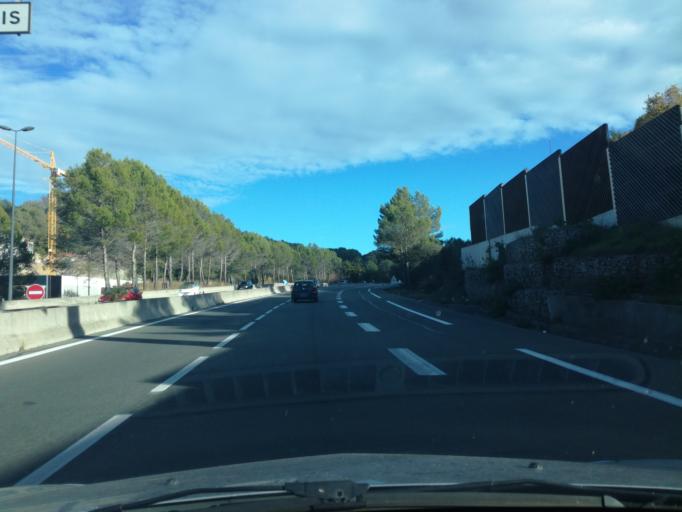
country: FR
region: Provence-Alpes-Cote d'Azur
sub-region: Departement des Alpes-Maritimes
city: Mouans-Sartoux
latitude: 43.6077
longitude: 6.9833
